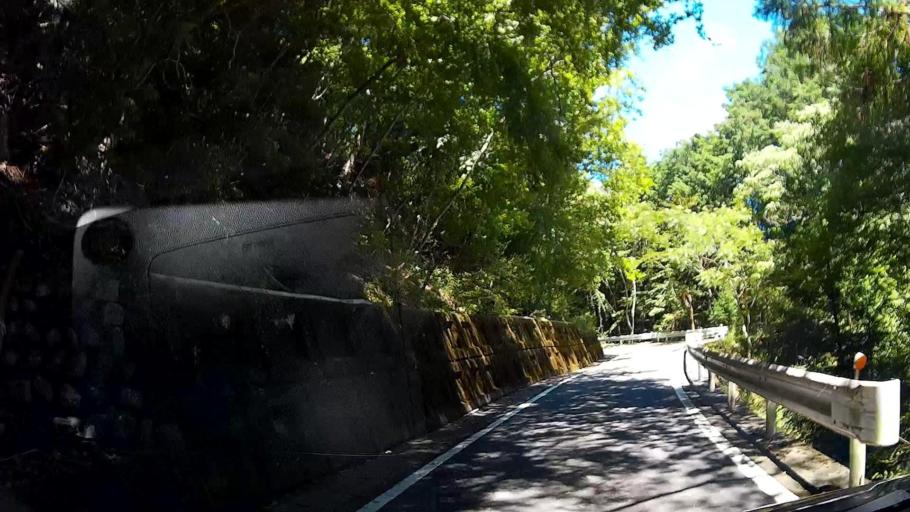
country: JP
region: Shizuoka
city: Shizuoka-shi
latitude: 35.1874
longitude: 138.2641
